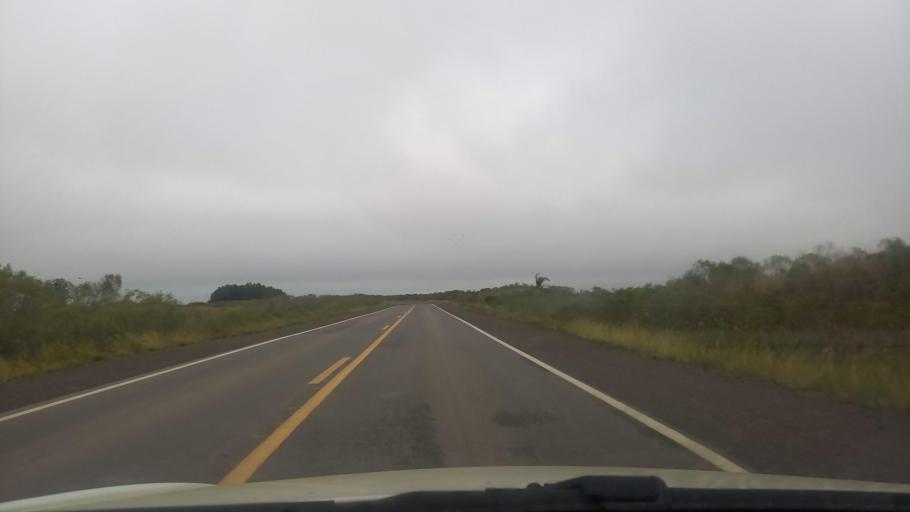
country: BR
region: Rio Grande do Sul
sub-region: Cacequi
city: Cacequi
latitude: -30.0683
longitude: -54.6141
